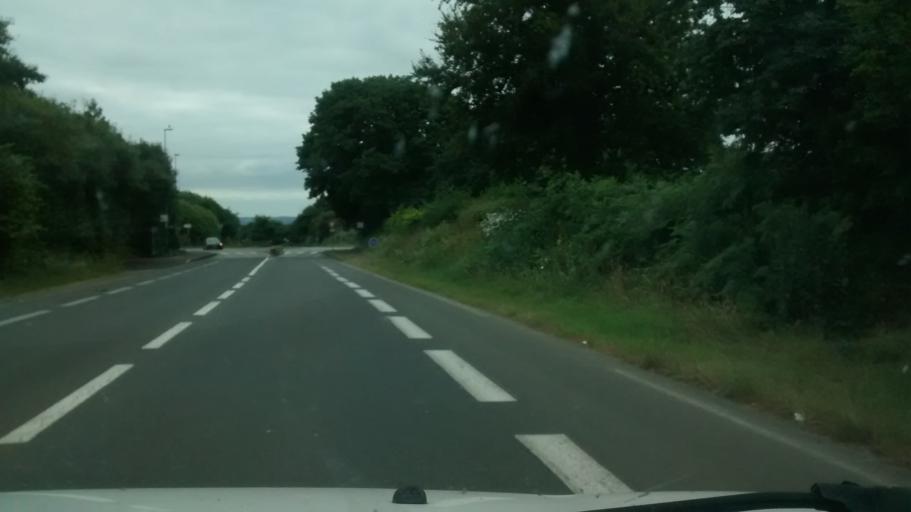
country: FR
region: Brittany
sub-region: Departement du Finistere
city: Plougastel-Daoulas
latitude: 48.3732
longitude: -4.3801
